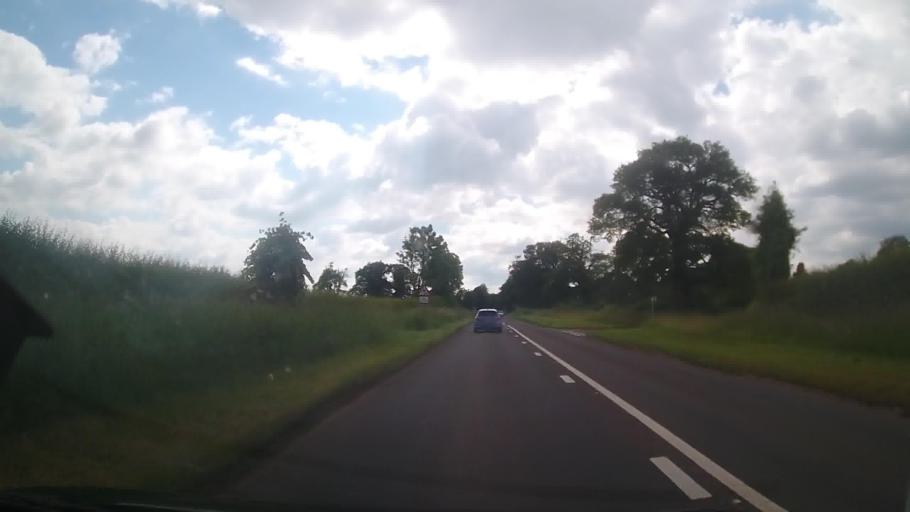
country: GB
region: England
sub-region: Shropshire
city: Ellesmere
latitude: 52.8996
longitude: -2.9198
